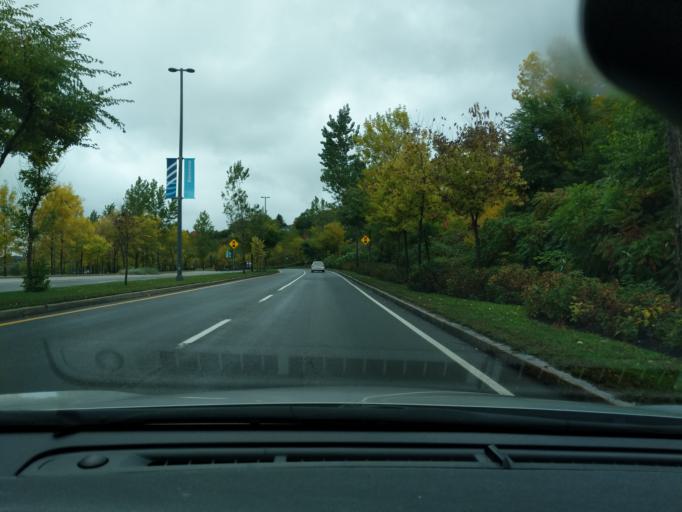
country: CA
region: Quebec
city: Quebec
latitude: 46.7592
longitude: -71.2683
